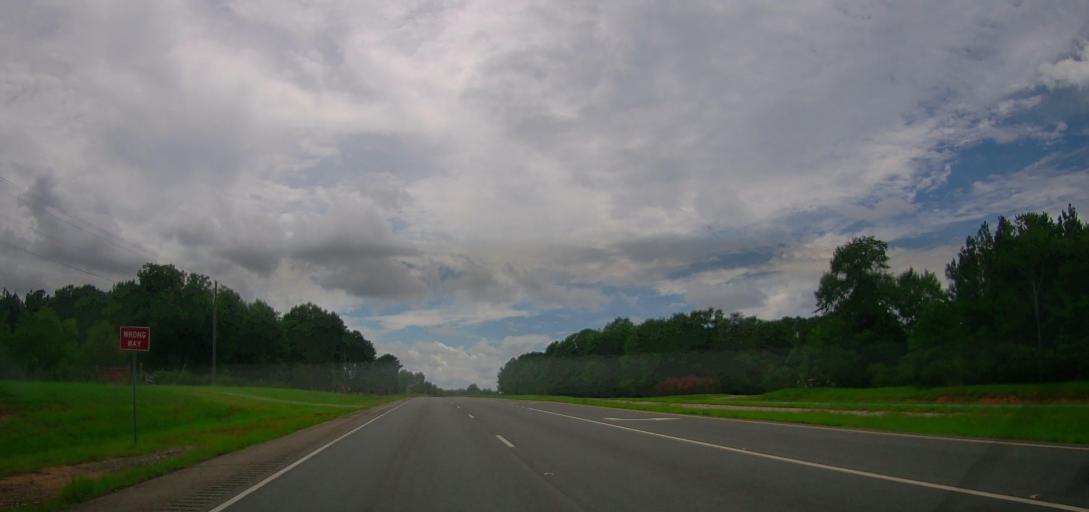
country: US
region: Georgia
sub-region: Telfair County
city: Helena
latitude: 32.1044
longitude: -82.9898
